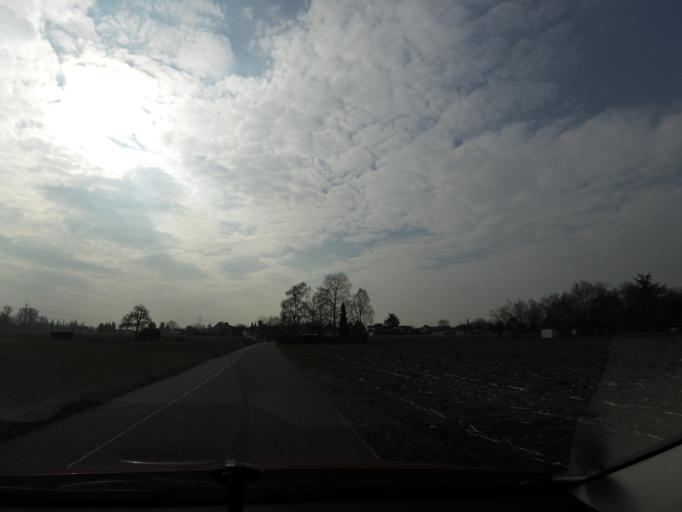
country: DE
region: Baden-Wuerttemberg
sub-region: Freiburg Region
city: Kehl
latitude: 48.5927
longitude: 7.8674
